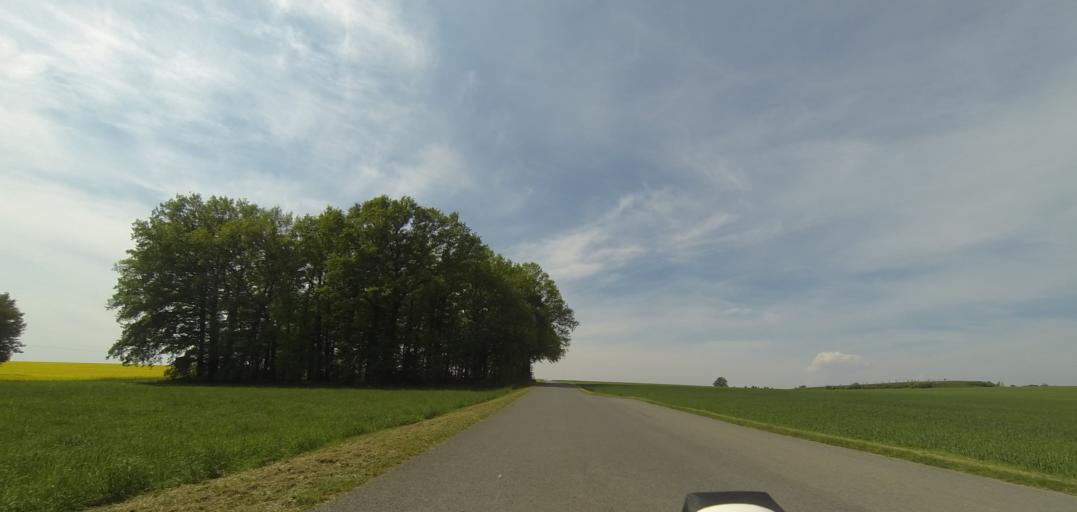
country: DE
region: Saxony
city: Arnsdorf
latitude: 51.0835
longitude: 13.9446
